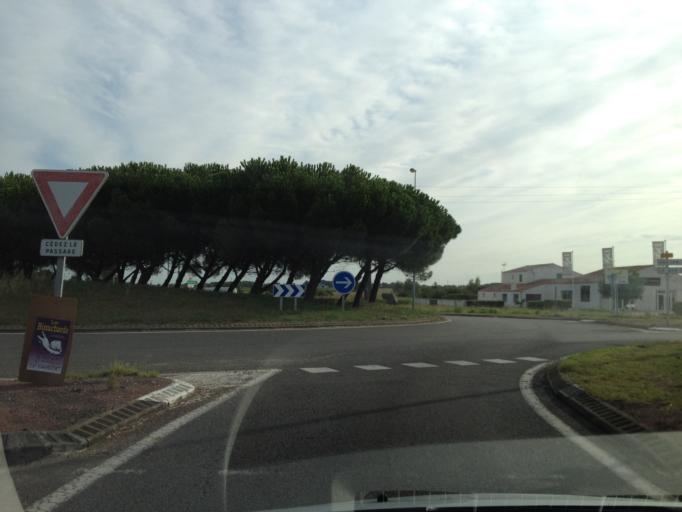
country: FR
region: Poitou-Charentes
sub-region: Departement de la Charente-Maritime
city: Le Gua
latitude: 45.7314
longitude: -0.9564
